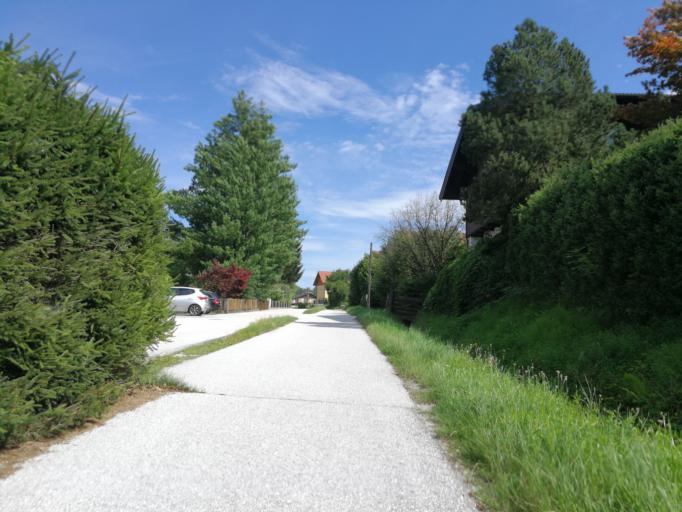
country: AT
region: Salzburg
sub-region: Politischer Bezirk Salzburg-Umgebung
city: Eugendorf
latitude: 47.8611
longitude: 13.1454
